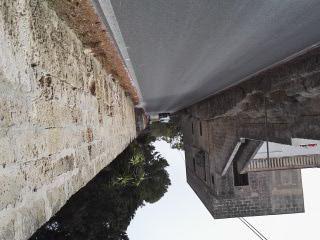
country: IT
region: Sicily
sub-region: Trapani
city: Favignana
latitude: 37.9253
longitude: 12.3358
